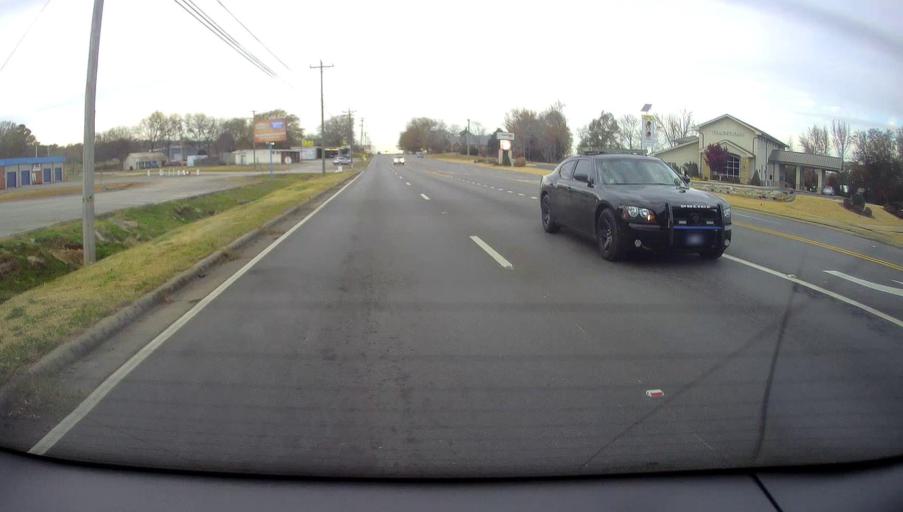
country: US
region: Alabama
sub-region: Morgan County
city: Priceville
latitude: 34.5253
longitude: -86.8952
